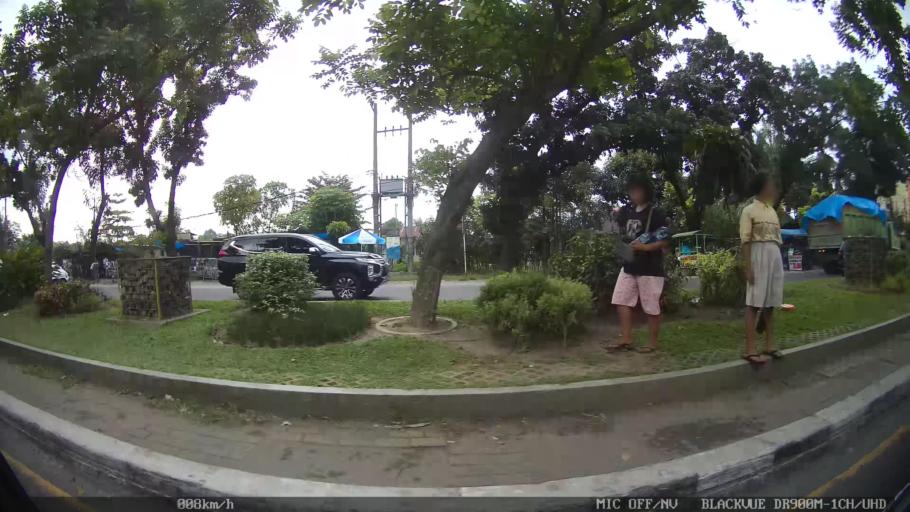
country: ID
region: North Sumatra
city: Deli Tua
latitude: 3.5416
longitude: 98.6637
